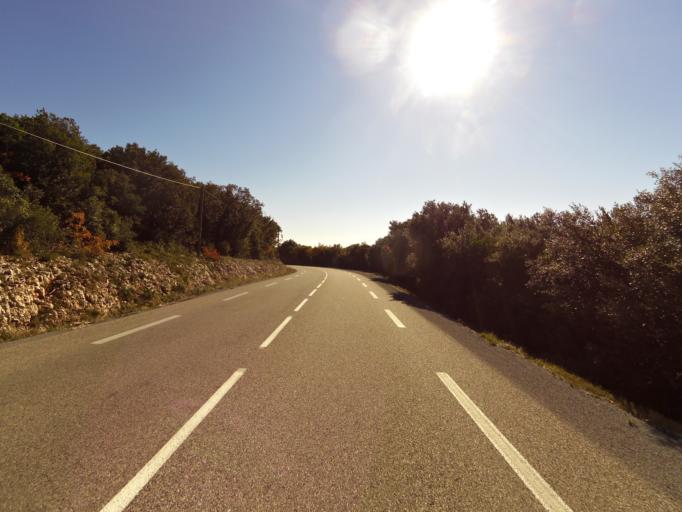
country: FR
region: Rhone-Alpes
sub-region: Departement de l'Ardeche
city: Ruoms
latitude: 44.4020
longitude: 4.4697
